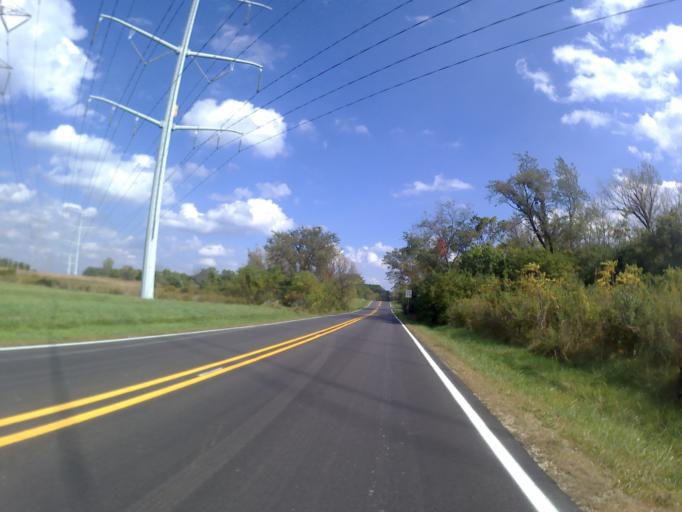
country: US
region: Illinois
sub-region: DuPage County
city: Woodridge
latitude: 41.7421
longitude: -88.0841
